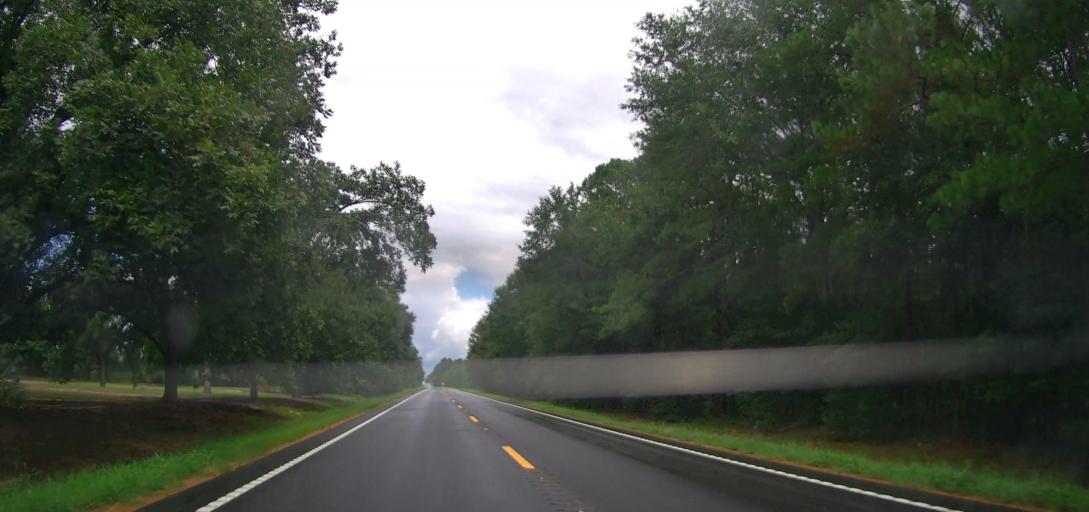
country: US
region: Georgia
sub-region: Wilcox County
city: Rochelle
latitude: 32.1007
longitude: -83.5829
